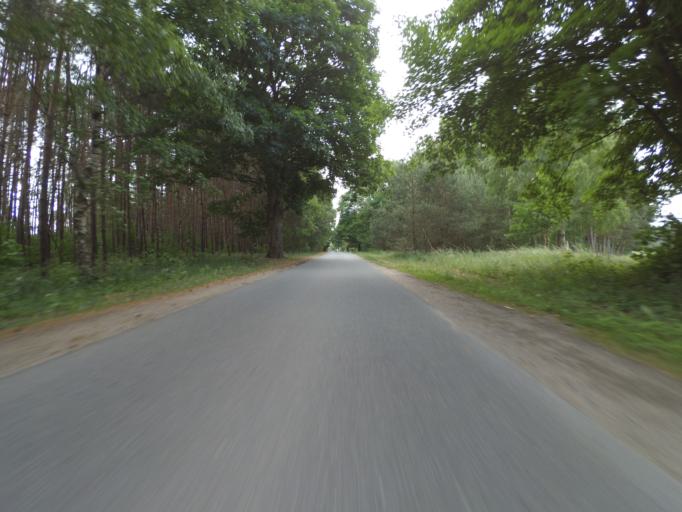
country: DE
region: Mecklenburg-Vorpommern
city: Malchow
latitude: 53.5399
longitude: 12.4230
